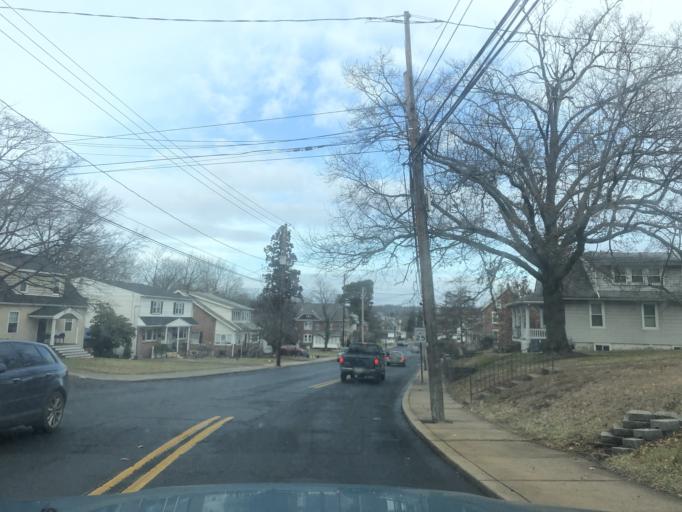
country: US
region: Pennsylvania
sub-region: Bucks County
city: Sellersville
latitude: 40.3517
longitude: -75.3050
